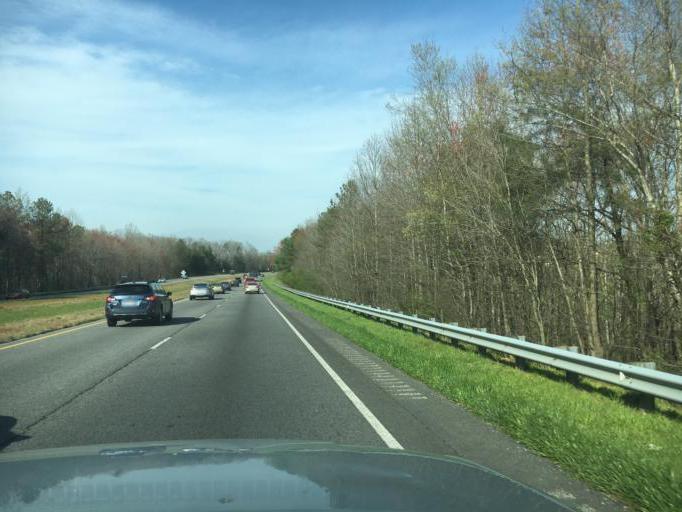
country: US
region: Georgia
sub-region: Habersham County
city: Baldwin
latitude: 34.5048
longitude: -83.5685
